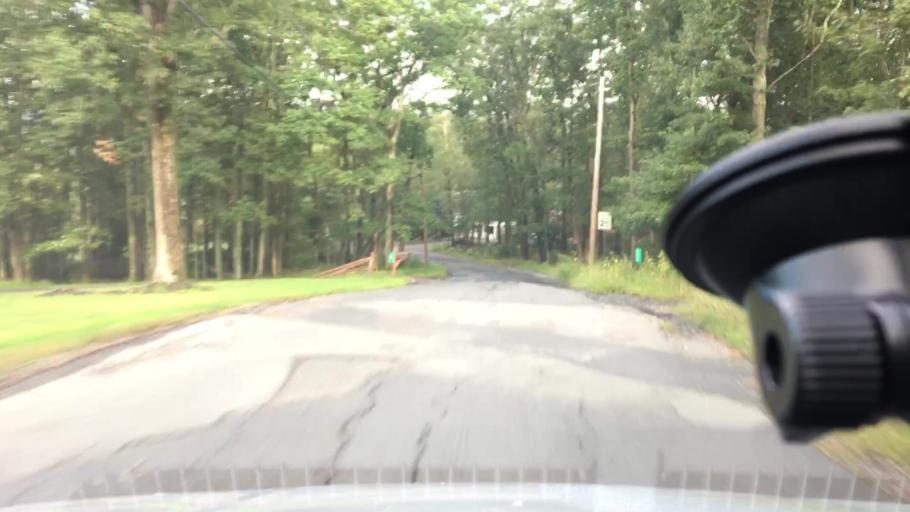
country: US
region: Pennsylvania
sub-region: Monroe County
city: Mountainhome
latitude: 41.1586
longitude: -75.2584
